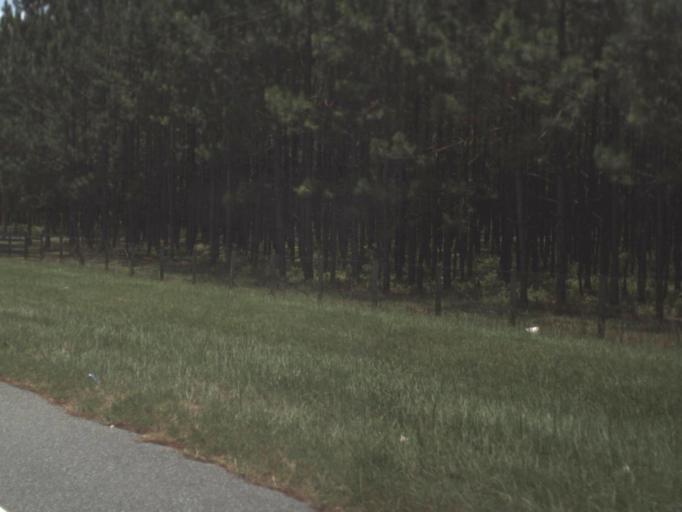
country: US
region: Florida
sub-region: Alachua County
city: High Springs
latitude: 30.0039
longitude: -82.5866
